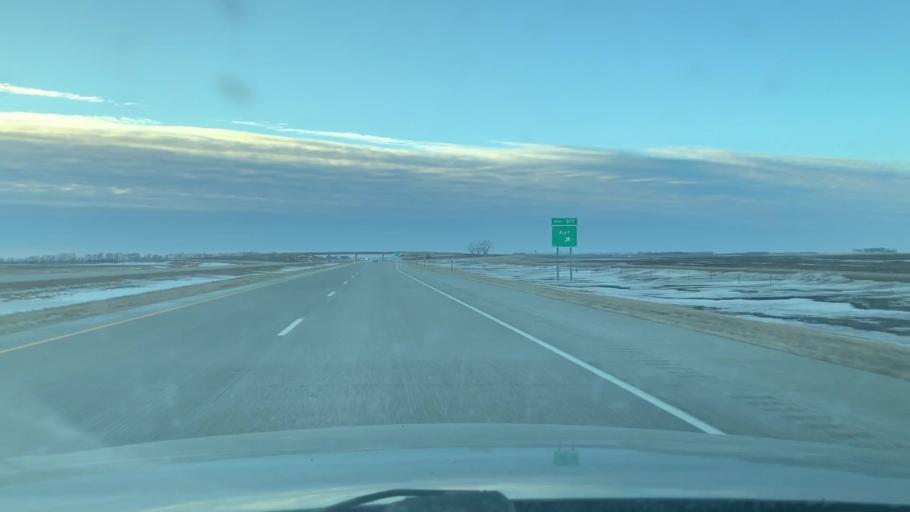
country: US
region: North Dakota
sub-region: Cass County
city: Casselton
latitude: 46.8758
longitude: -97.4851
